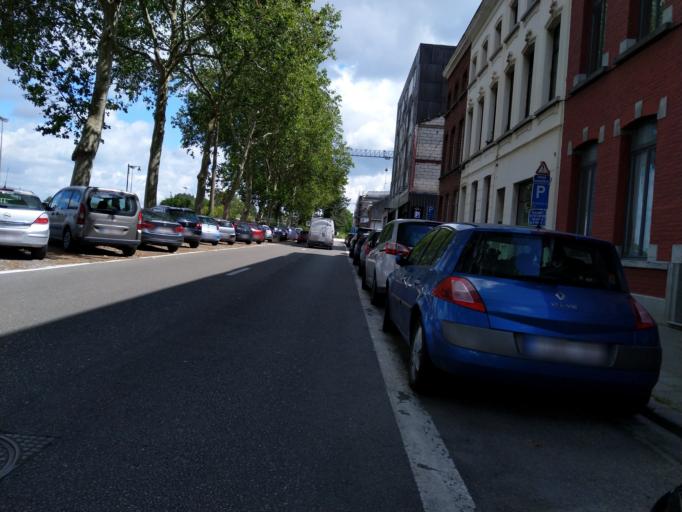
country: BE
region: Wallonia
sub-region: Province du Hainaut
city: Mons
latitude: 50.4573
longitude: 3.9468
